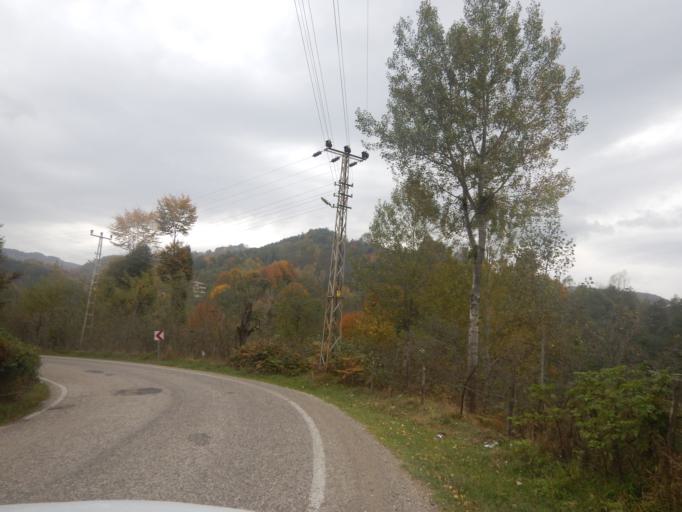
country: TR
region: Ordu
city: Golkoy
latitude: 40.6842
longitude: 37.5659
